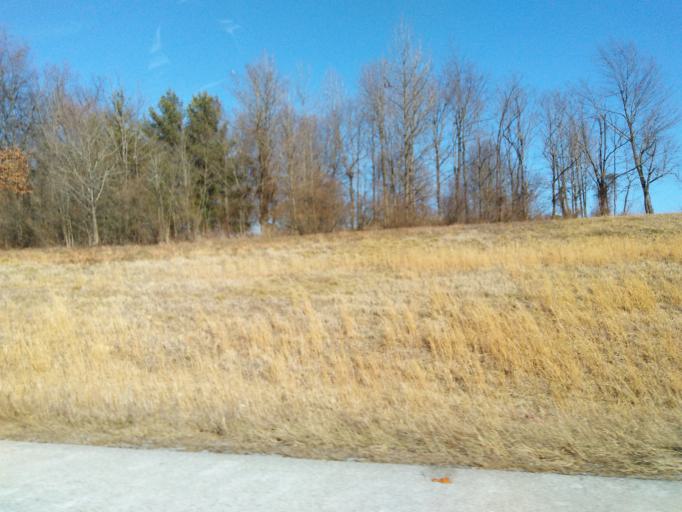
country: US
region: Illinois
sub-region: Massac County
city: Metropolis
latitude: 37.2187
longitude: -88.7016
